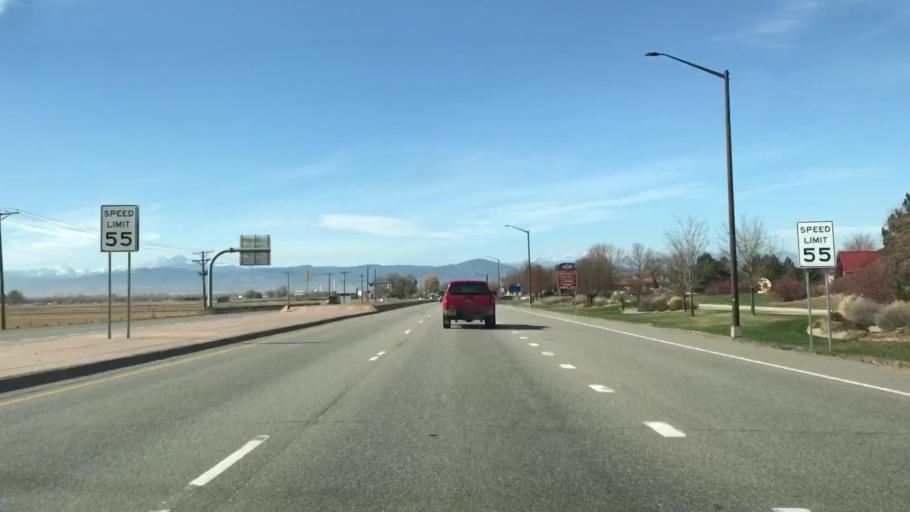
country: US
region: Colorado
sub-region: Larimer County
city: Loveland
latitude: 40.4073
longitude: -104.9991
